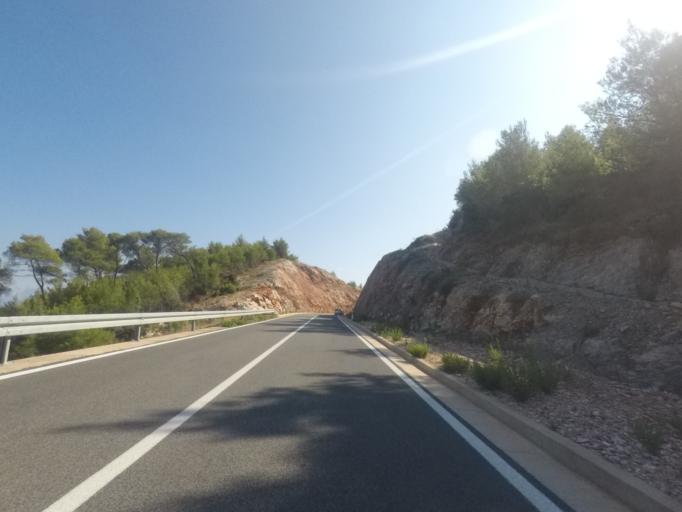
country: HR
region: Splitsko-Dalmatinska
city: Jelsa
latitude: 43.1524
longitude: 16.7194
